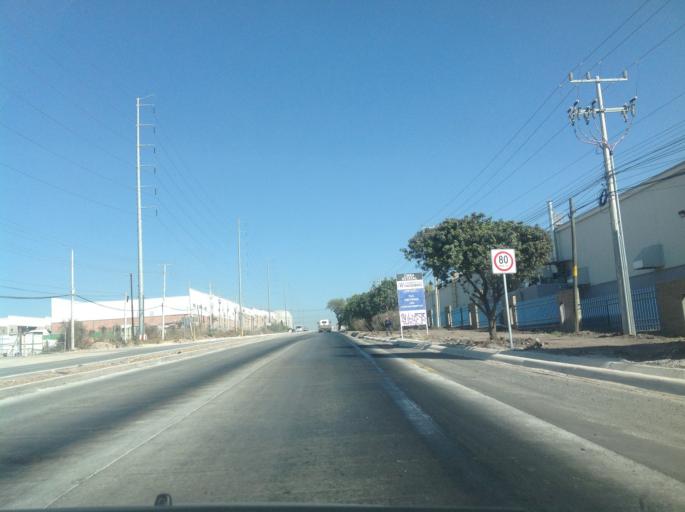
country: MX
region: Queretaro
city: El Colorado
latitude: 20.5577
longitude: -100.2673
